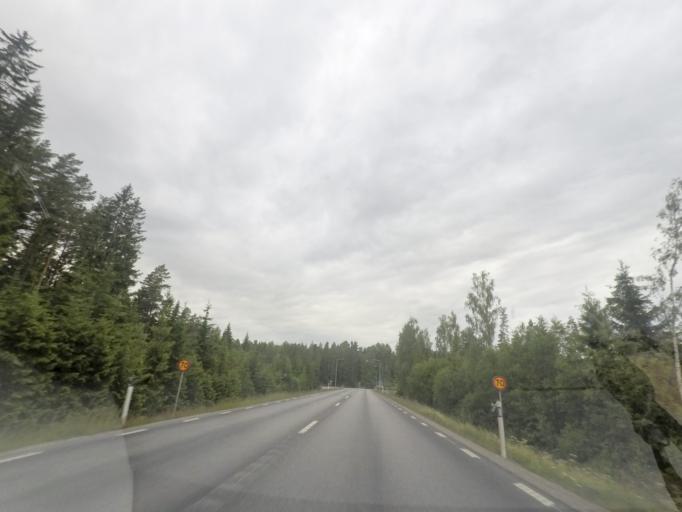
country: SE
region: OErebro
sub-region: Lindesbergs Kommun
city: Lindesberg
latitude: 59.5546
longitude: 15.2259
